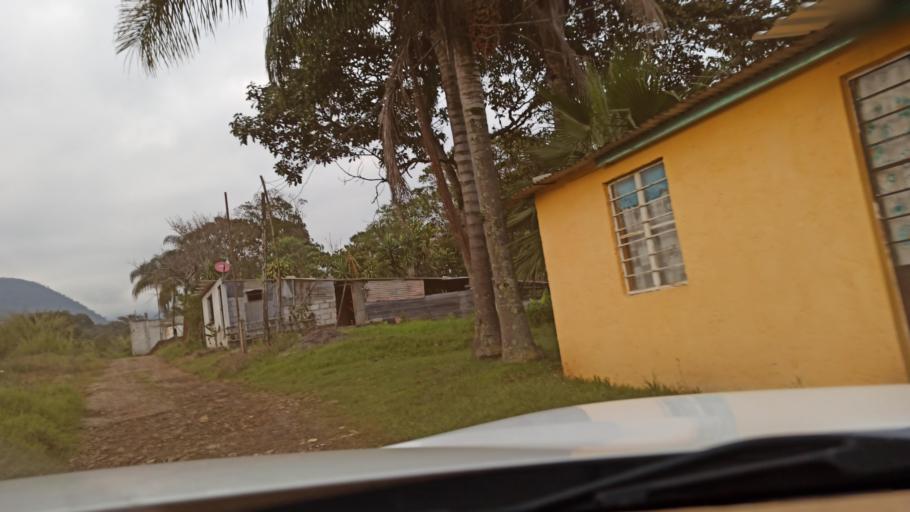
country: MX
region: Veracruz
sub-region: Fortin
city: Monte Salas
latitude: 18.9253
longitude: -97.0154
